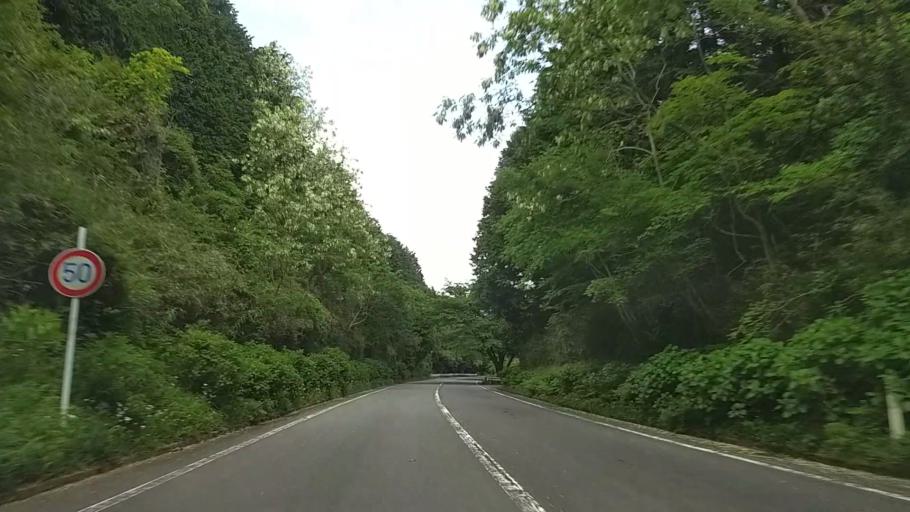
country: JP
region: Kanagawa
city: Odawara
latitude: 35.2255
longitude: 139.1170
